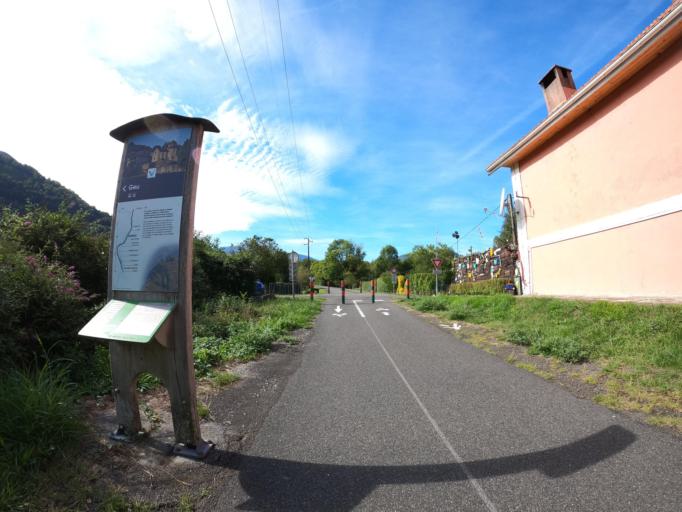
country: FR
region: Midi-Pyrenees
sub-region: Departement des Hautes-Pyrenees
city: Argeles-Gazost
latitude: 43.0424
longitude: -0.0580
